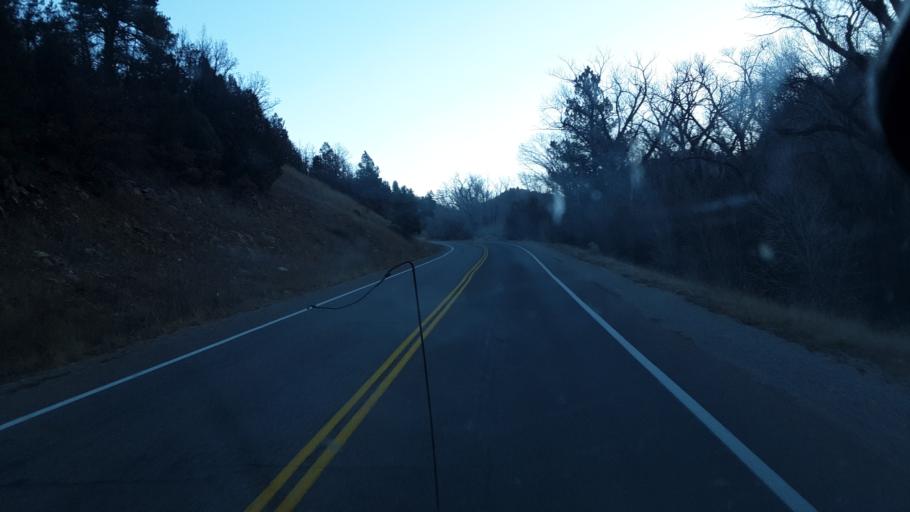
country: US
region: Colorado
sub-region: La Plata County
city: Durango
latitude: 37.3055
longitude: -107.8259
